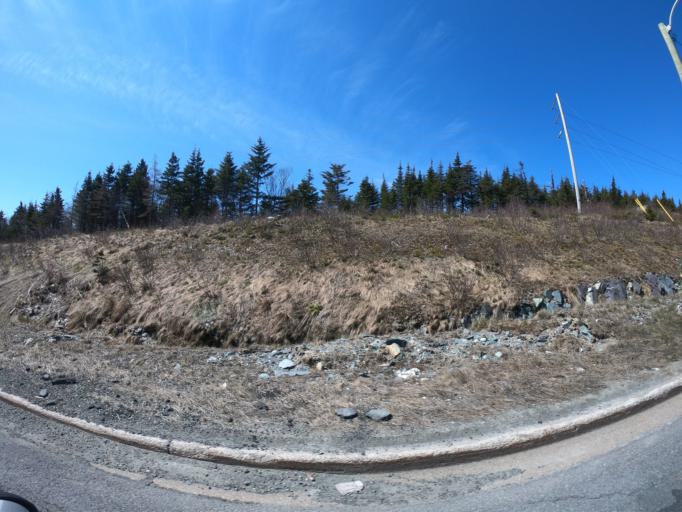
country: CA
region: Newfoundland and Labrador
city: Mount Pearl
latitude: 47.5064
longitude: -52.8227
